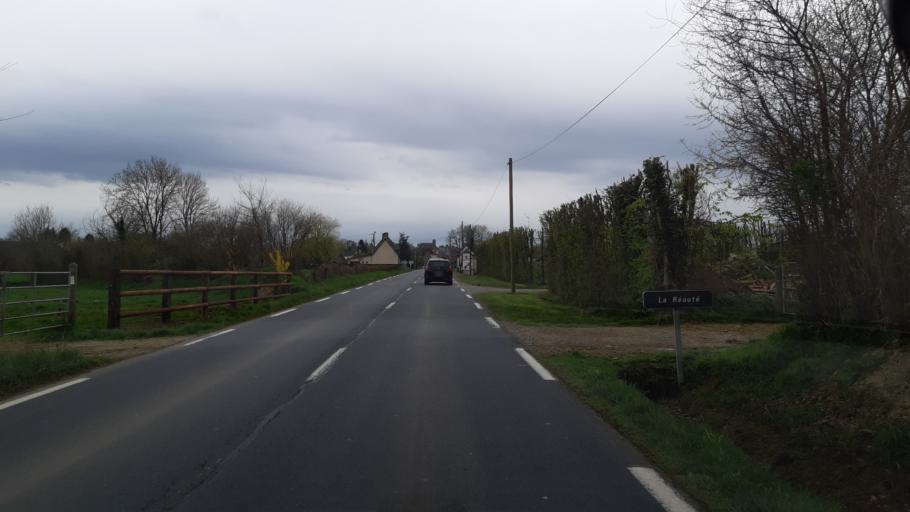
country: FR
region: Lower Normandy
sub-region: Departement de la Manche
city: Percy
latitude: 48.9701
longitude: -1.1635
